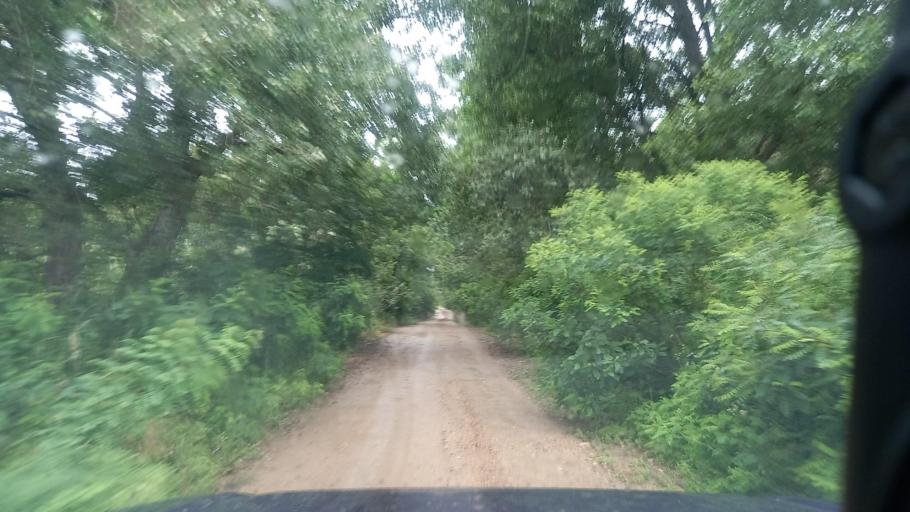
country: RU
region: Krasnodarskiy
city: Vasyurinskaya
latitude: 45.0311
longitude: 39.4750
